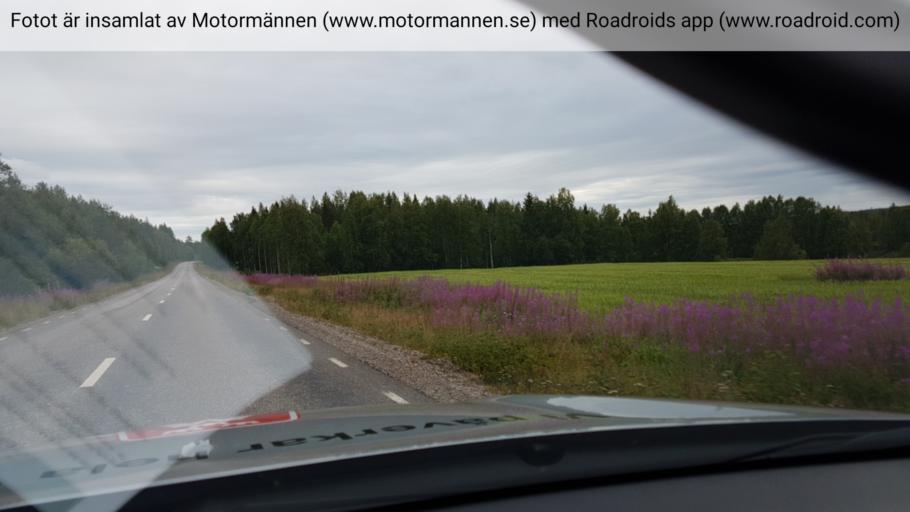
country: SE
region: Norrbotten
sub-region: Overkalix Kommun
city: OEverkalix
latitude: 66.4993
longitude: 22.7704
